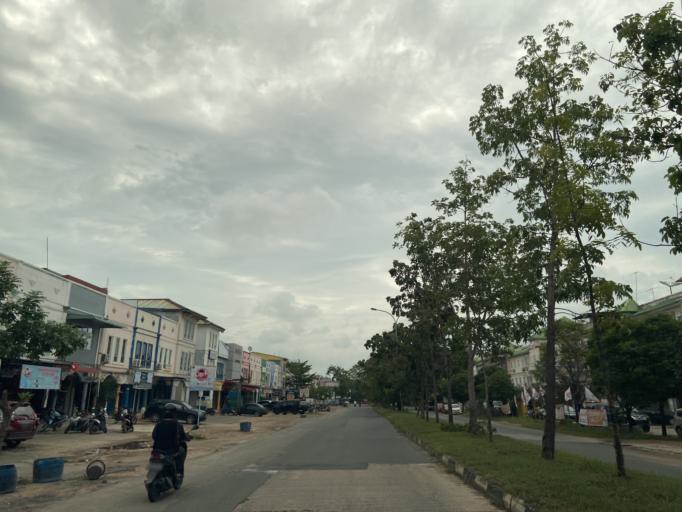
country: SG
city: Singapore
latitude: 1.1243
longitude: 104.0472
